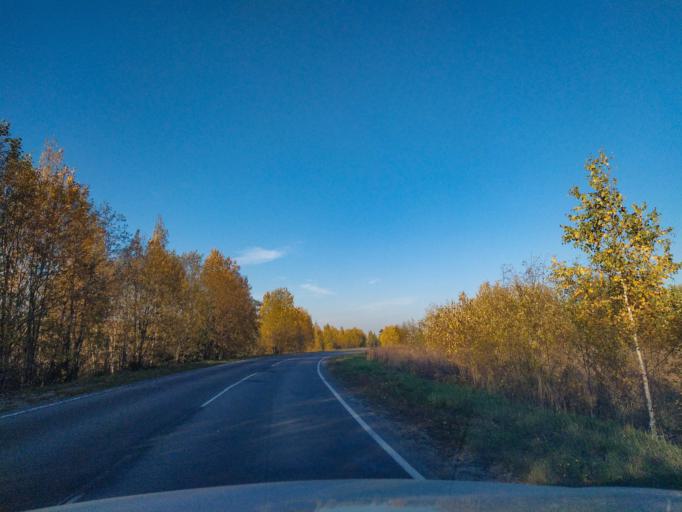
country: RU
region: Leningrad
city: Siverskiy
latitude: 59.3098
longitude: 30.0293
